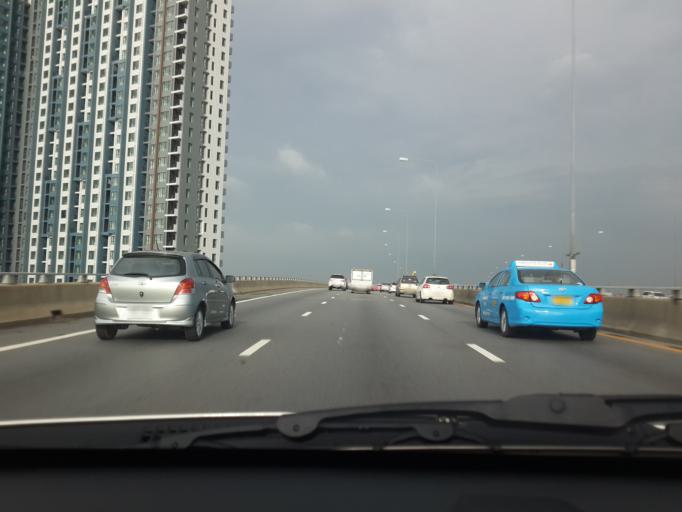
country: TH
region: Bangkok
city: Watthana
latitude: 13.7482
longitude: 100.6039
